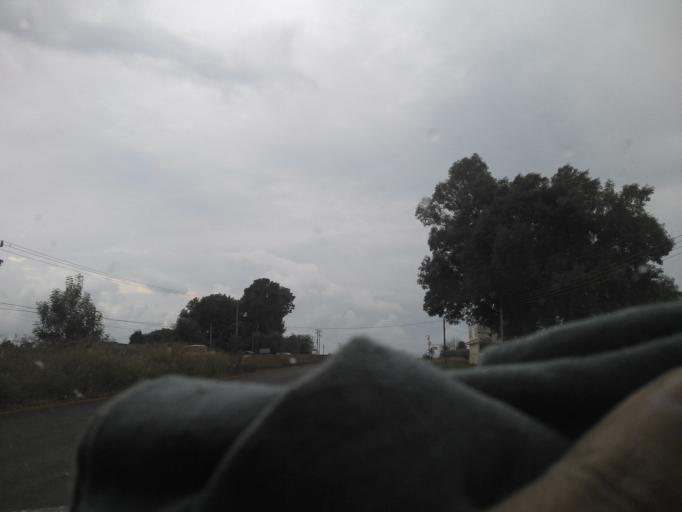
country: MX
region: Jalisco
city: Arandas
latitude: 20.7182
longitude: -102.4410
